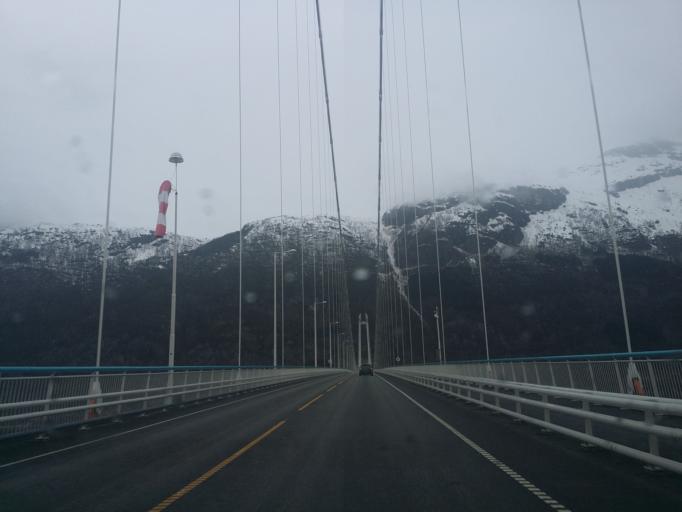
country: NO
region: Hordaland
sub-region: Ulvik
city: Ulvik
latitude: 60.4735
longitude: 6.8361
